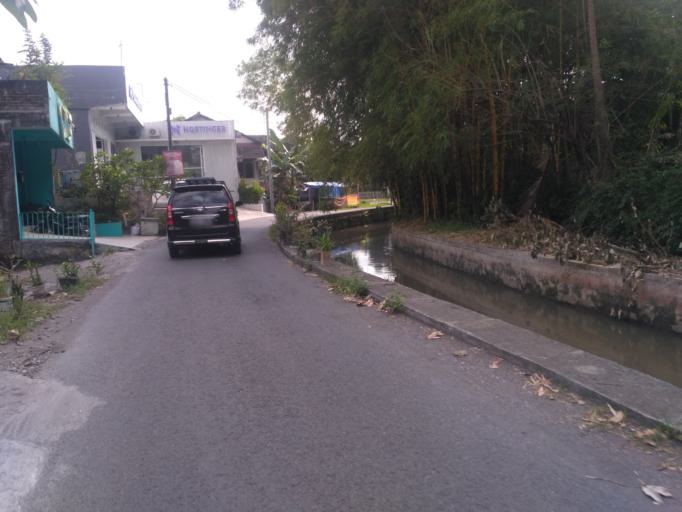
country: ID
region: Daerah Istimewa Yogyakarta
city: Yogyakarta
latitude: -7.7591
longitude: 110.3687
